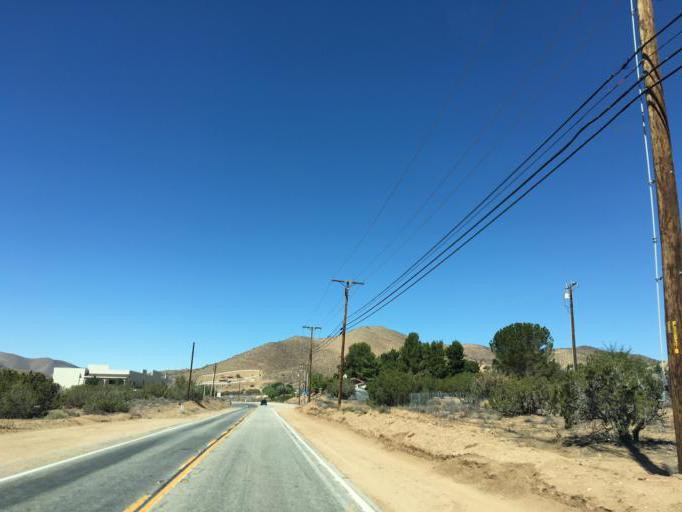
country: US
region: California
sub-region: Los Angeles County
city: Acton
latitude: 34.4809
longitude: -118.1611
